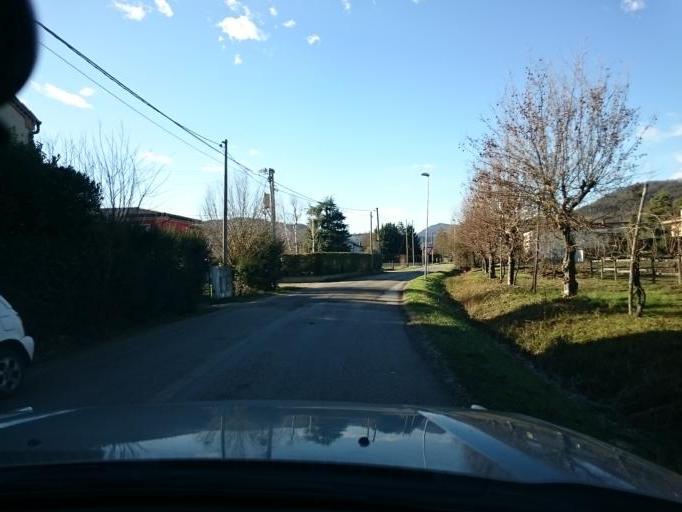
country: IT
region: Veneto
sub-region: Provincia di Padova
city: Torreglia
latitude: 45.3385
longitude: 11.7444
